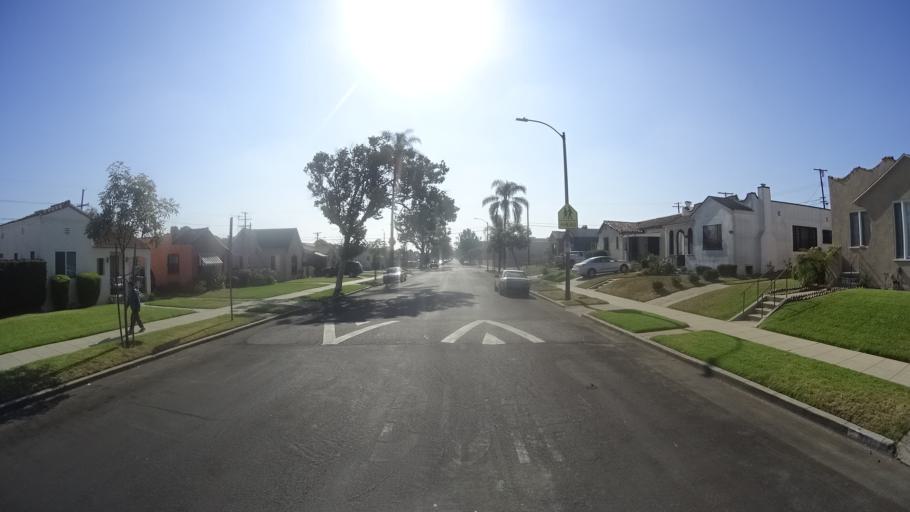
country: US
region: California
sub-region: Los Angeles County
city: Westmont
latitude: 33.9777
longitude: -118.3145
